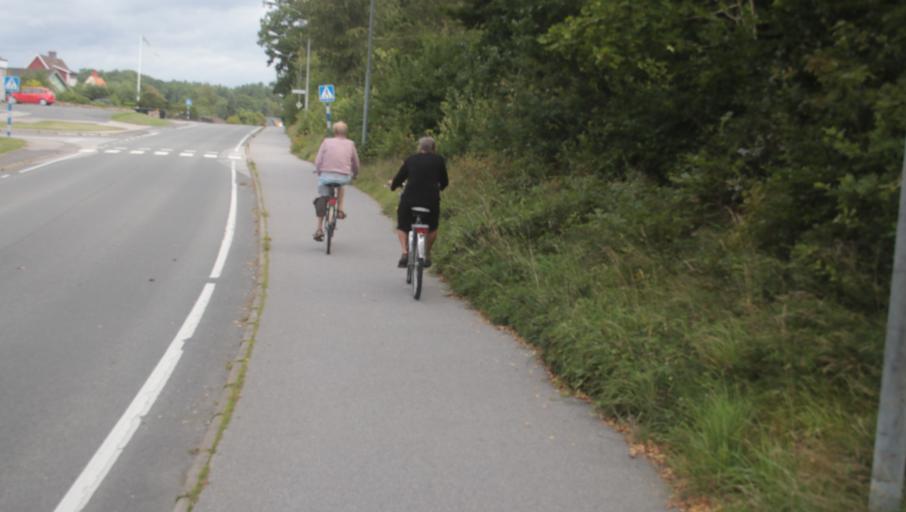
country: SE
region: Blekinge
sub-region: Karlshamns Kommun
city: Karlshamn
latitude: 56.1817
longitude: 14.8629
